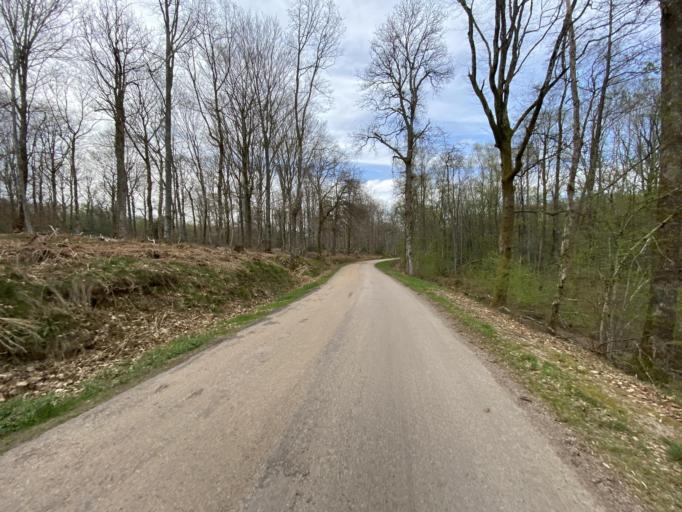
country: FR
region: Bourgogne
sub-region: Departement de la Cote-d'Or
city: Saulieu
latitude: 47.3012
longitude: 4.0886
